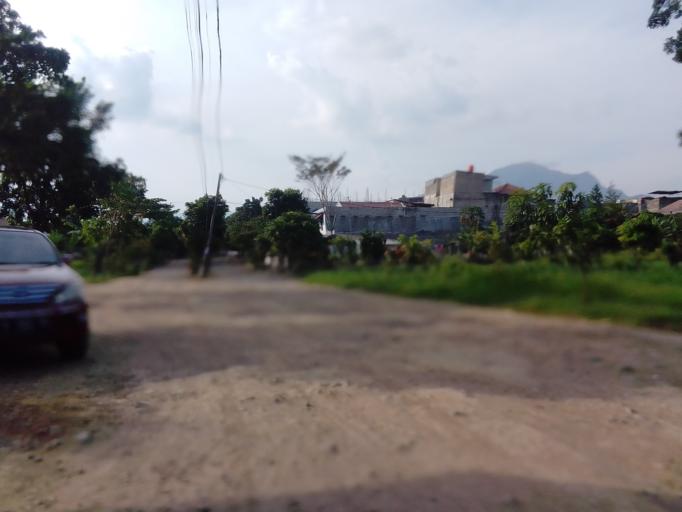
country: ID
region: West Java
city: Cileunyi
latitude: -6.9333
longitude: 107.7134
